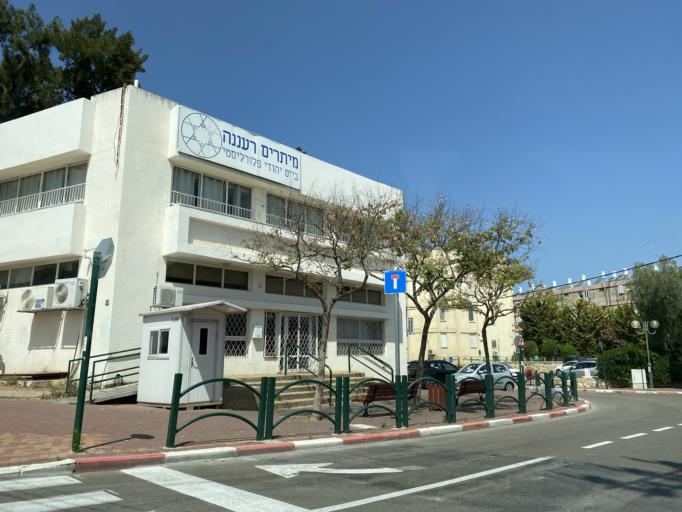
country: IL
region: Central District
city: Ra'anana
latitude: 32.1915
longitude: 34.8720
